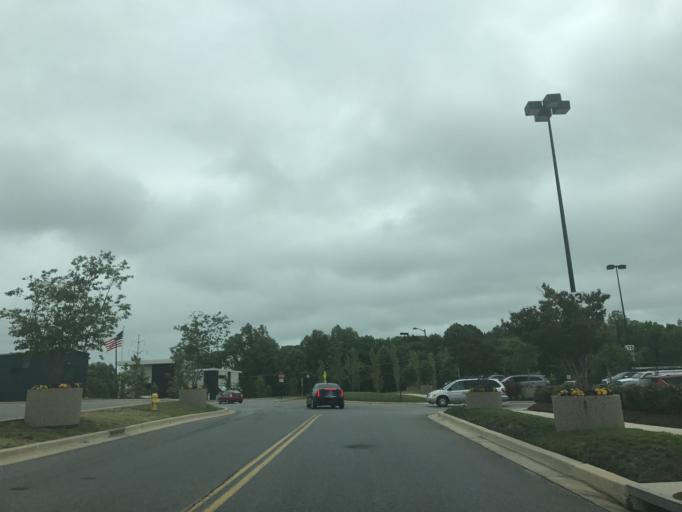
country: US
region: Maryland
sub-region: Anne Arundel County
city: Crofton
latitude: 39.0312
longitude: -76.6862
